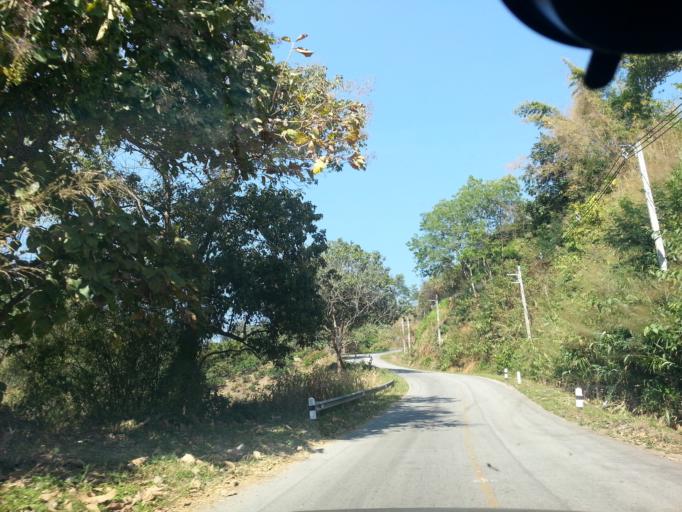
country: TH
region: Chiang Mai
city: Chai Prakan
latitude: 19.8249
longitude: 99.0988
